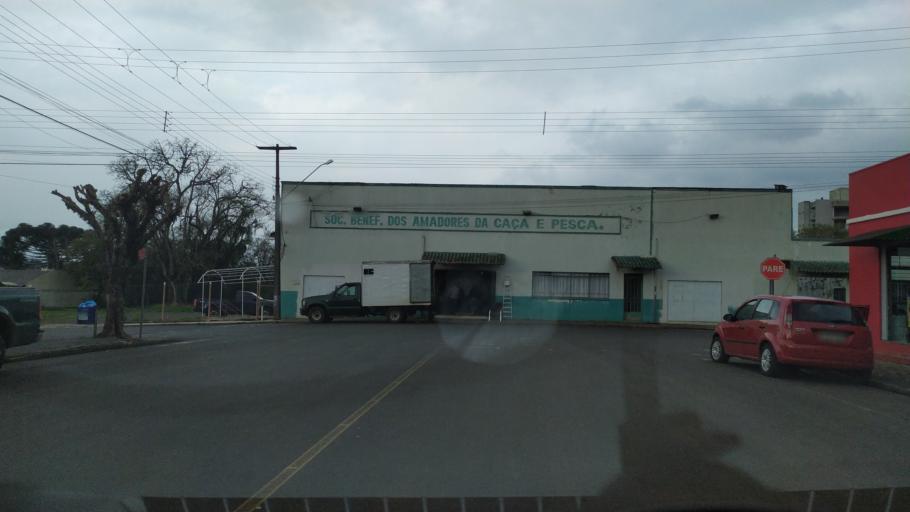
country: BR
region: Parana
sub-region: Palmas
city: Palmas
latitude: -26.4792
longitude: -51.9940
